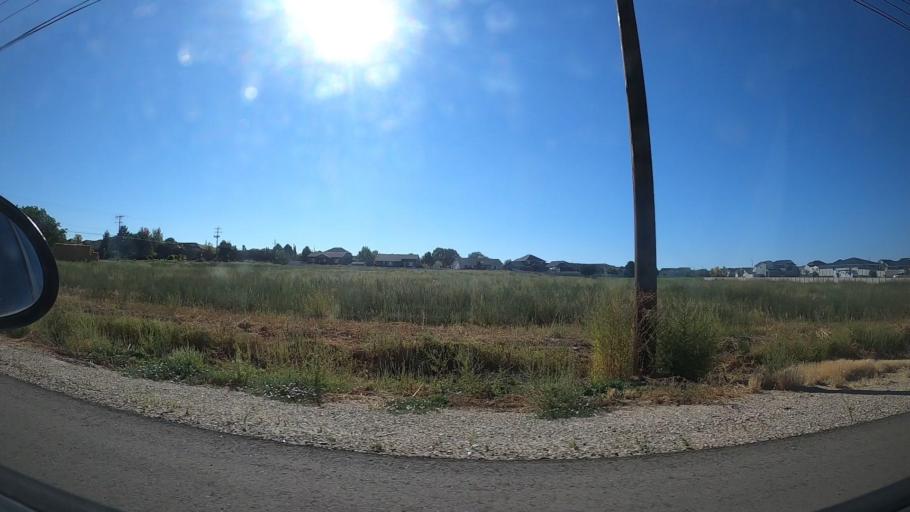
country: US
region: Idaho
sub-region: Canyon County
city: Nampa
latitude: 43.5576
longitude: -116.6128
